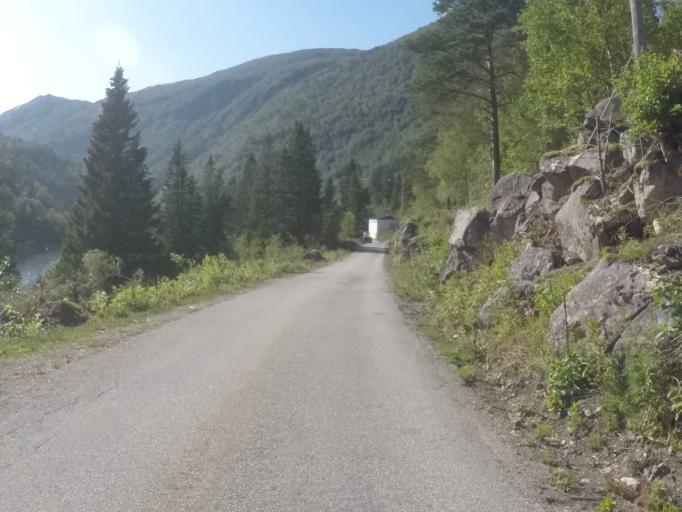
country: NO
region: Hordaland
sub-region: Odda
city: Odda
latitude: 60.1318
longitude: 6.6337
